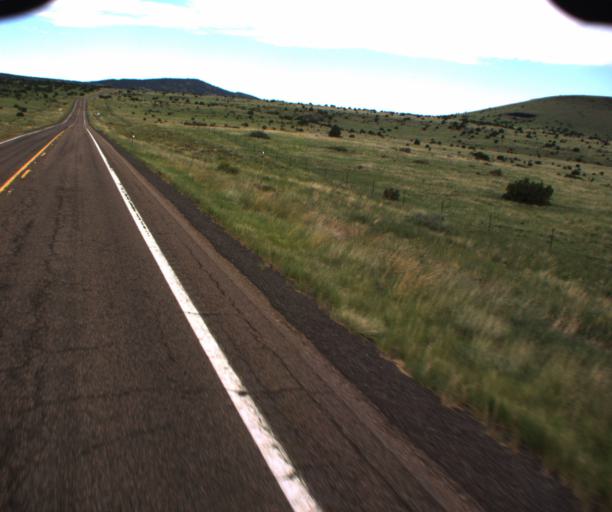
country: US
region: Arizona
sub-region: Apache County
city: Springerville
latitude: 34.2459
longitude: -109.5267
